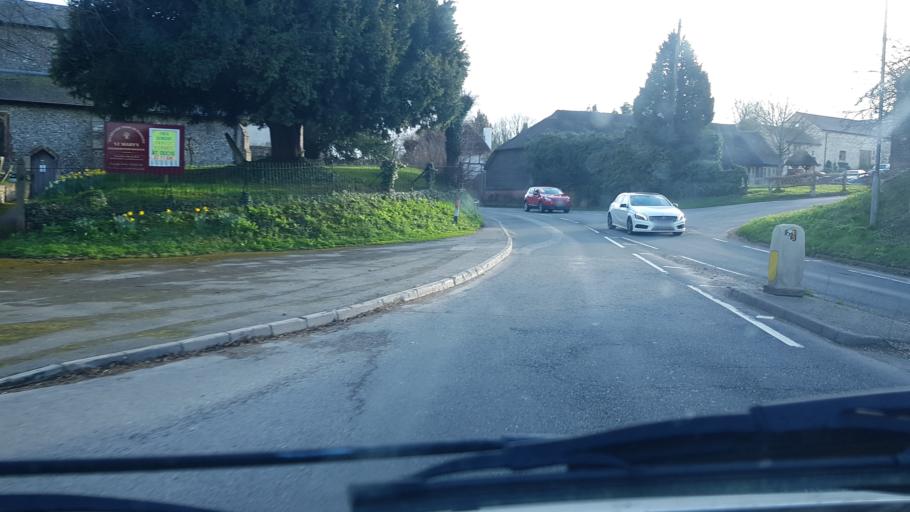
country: GB
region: England
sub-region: Wiltshire
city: Collingbourne Kingston
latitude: 51.3017
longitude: -1.6583
